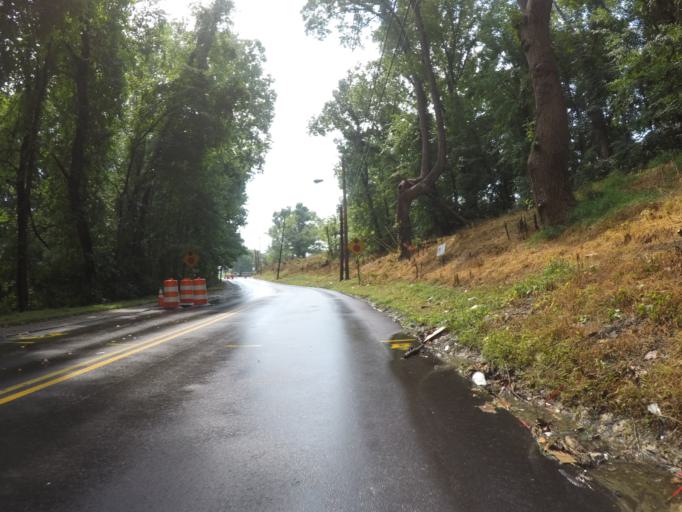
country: US
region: Kentucky
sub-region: Boyd County
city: Westwood
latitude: 38.4761
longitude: -82.6650
